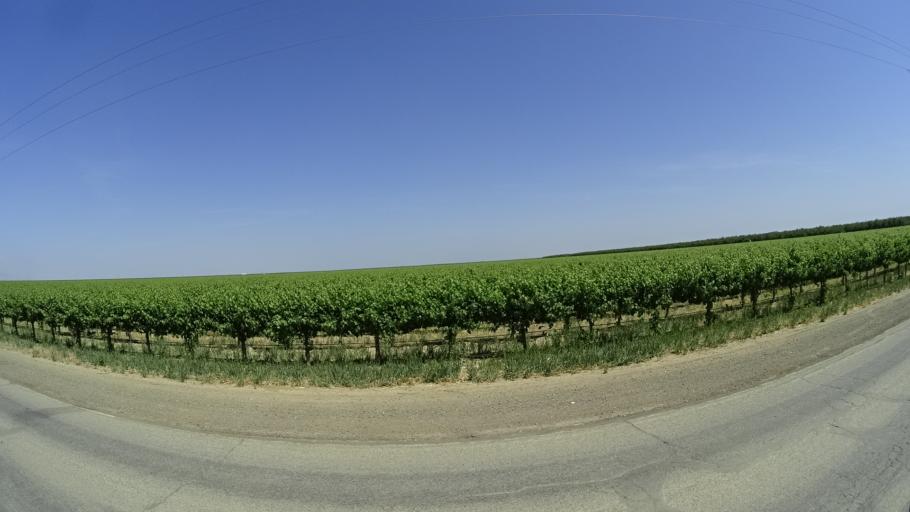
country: US
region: California
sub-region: Fresno County
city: Huron
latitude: 36.1377
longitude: -120.0061
